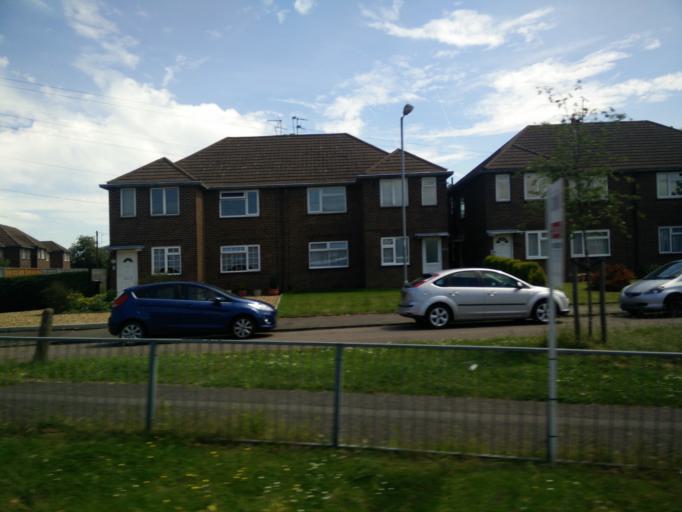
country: GB
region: England
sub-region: Luton
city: Luton
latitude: 51.9038
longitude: -0.3947
